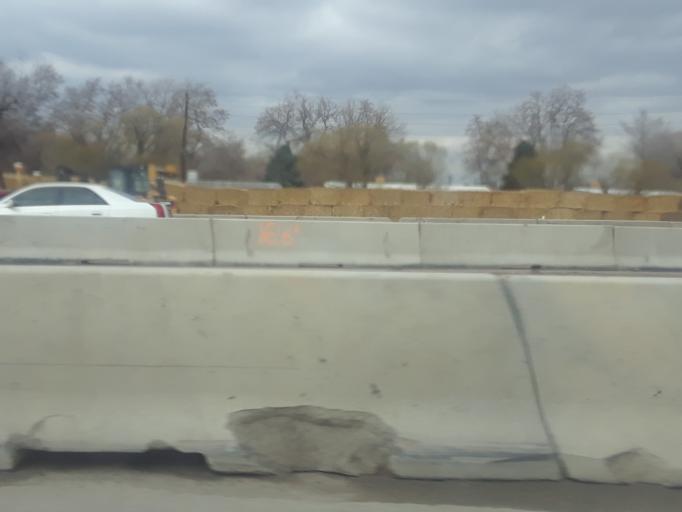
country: US
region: Colorado
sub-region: Arapahoe County
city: Columbine Valley
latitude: 39.5649
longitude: -105.0374
